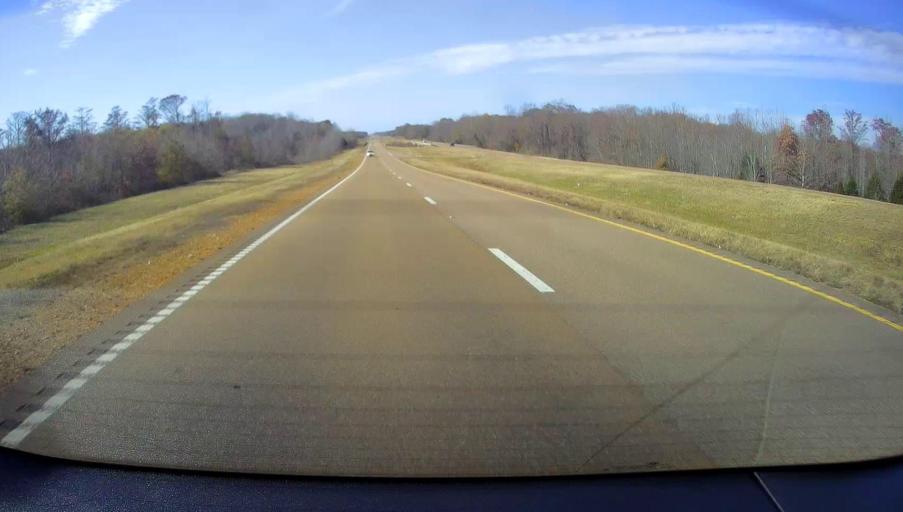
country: US
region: Mississippi
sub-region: Benton County
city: Ashland
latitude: 34.9459
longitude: -89.1915
